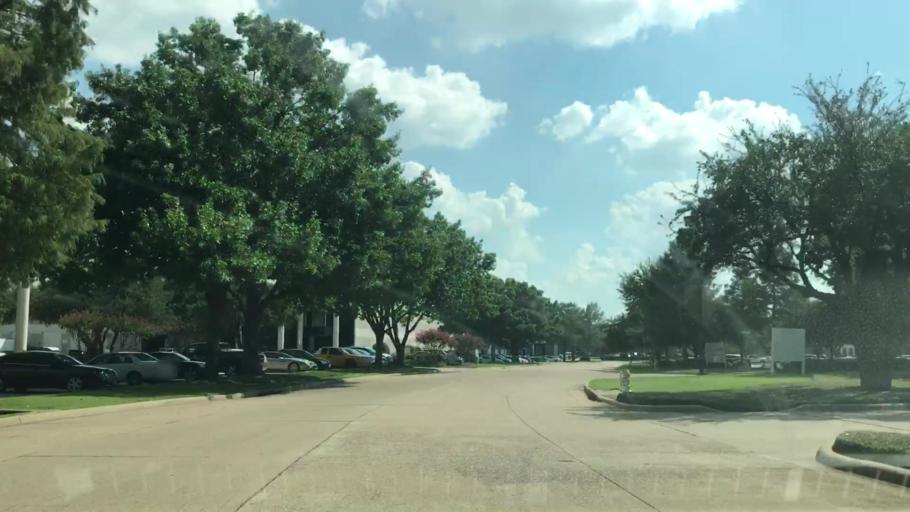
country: US
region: Texas
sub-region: Dallas County
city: Farmers Branch
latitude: 32.9436
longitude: -96.9210
